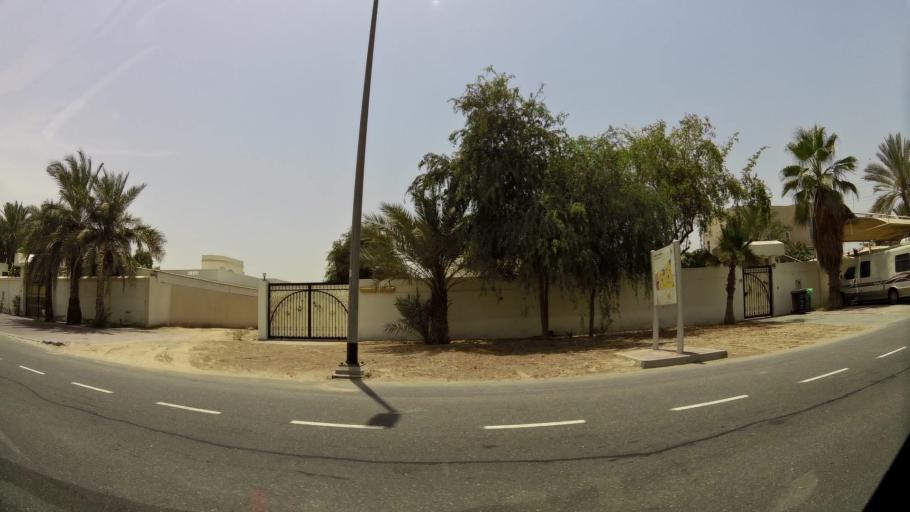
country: AE
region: Ash Shariqah
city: Sharjah
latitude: 25.2120
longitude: 55.3893
